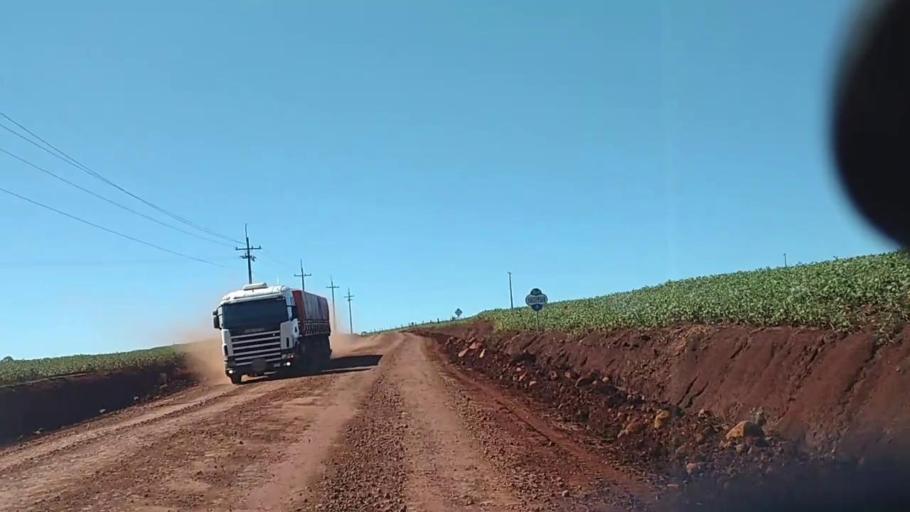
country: PY
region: Alto Parana
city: Naranjal
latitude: -25.9755
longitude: -55.2223
